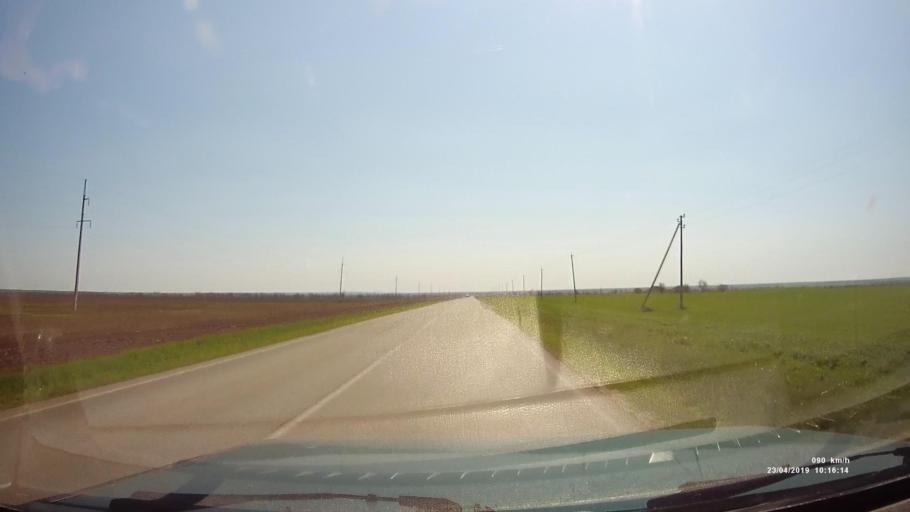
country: RU
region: Rostov
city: Sovetskoye
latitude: 46.6597
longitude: 42.3923
